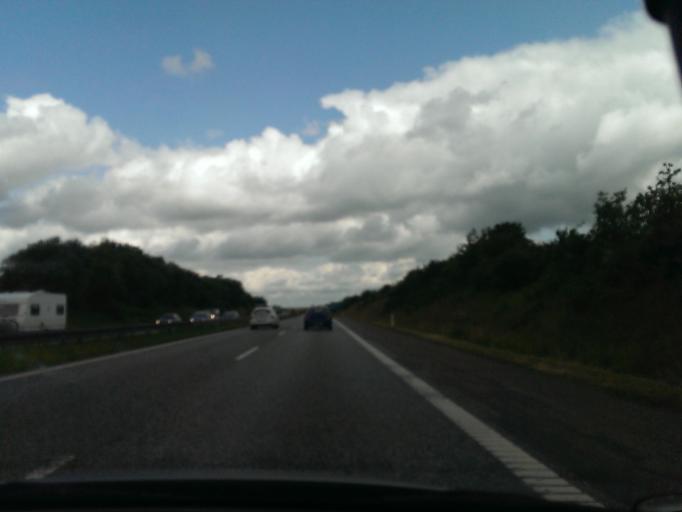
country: DK
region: North Denmark
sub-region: Mariagerfjord Kommune
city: Hobro
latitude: 56.5955
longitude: 9.7636
